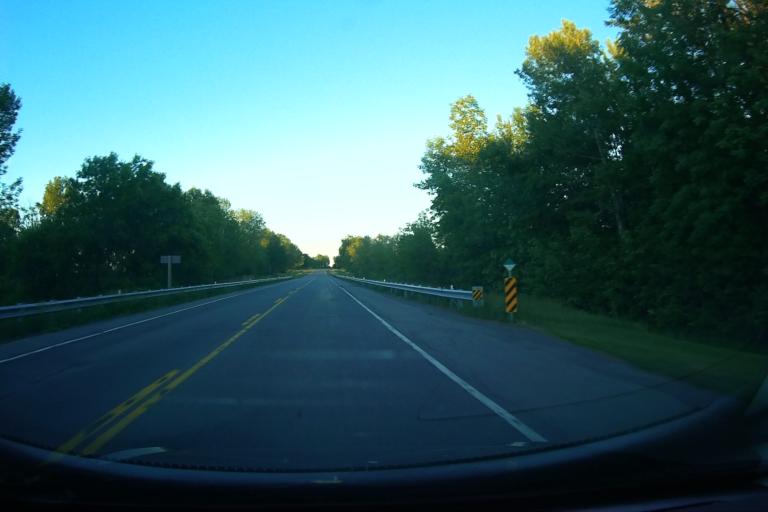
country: CA
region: Ontario
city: Casselman
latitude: 45.1026
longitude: -75.2519
